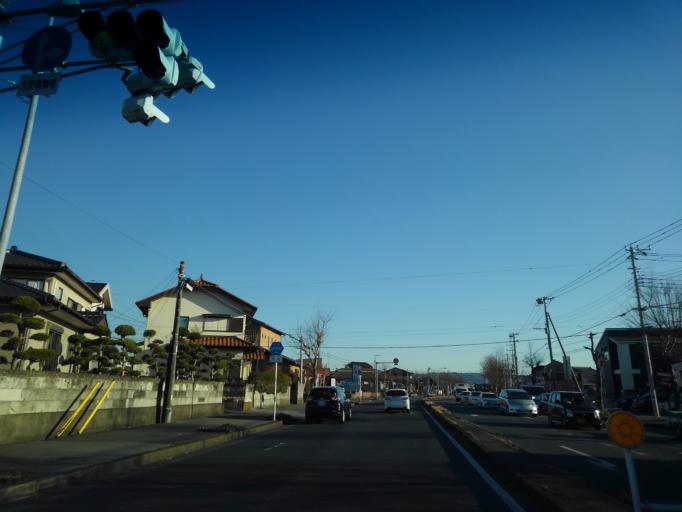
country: JP
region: Chiba
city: Kimitsu
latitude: 35.3242
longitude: 139.9104
